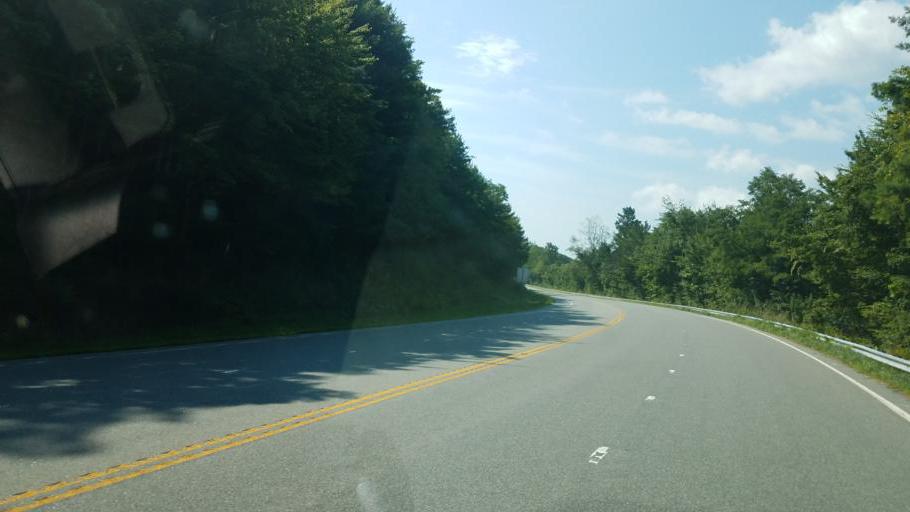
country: US
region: North Carolina
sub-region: Avery County
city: Newland
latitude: 35.9469
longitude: -81.8451
